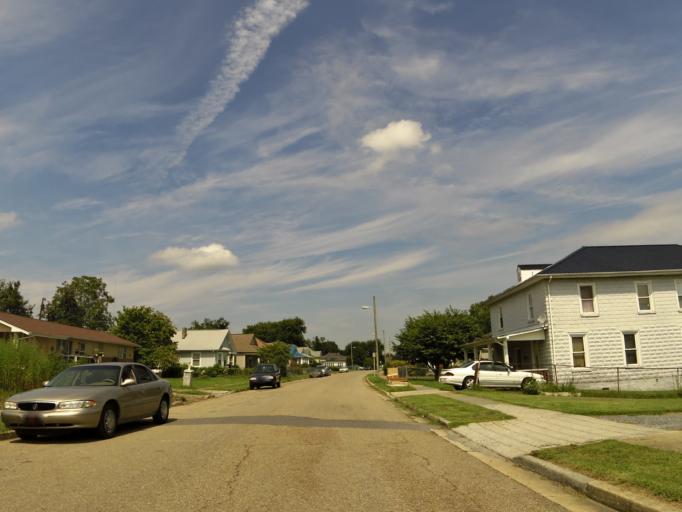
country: US
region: Tennessee
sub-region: Sullivan County
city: Kingsport
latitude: 36.5389
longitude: -82.5499
